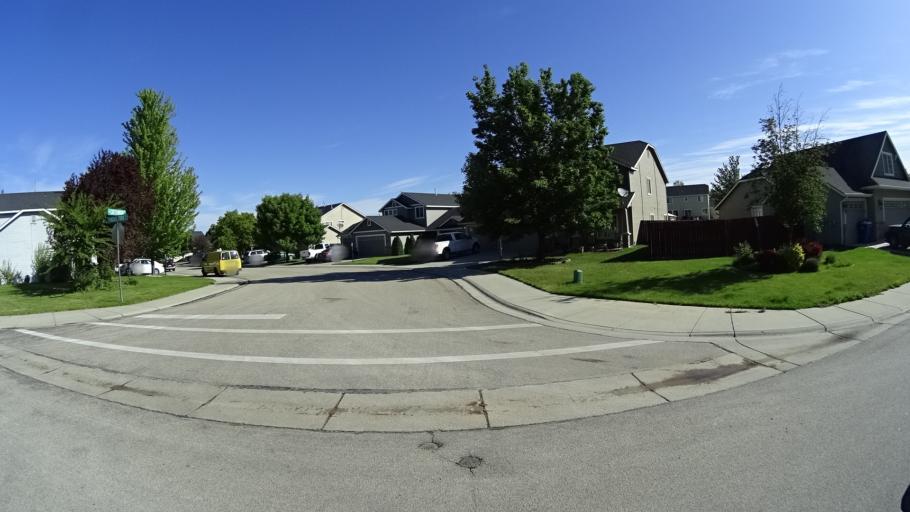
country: US
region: Idaho
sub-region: Ada County
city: Garden City
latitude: 43.5687
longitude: -116.2763
